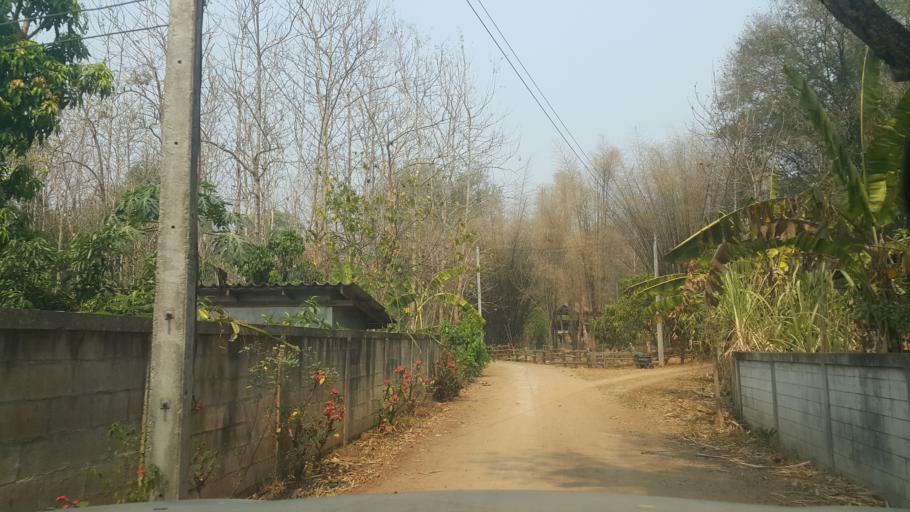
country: TH
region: Lampang
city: Sop Prap
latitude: 17.8066
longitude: 99.2562
